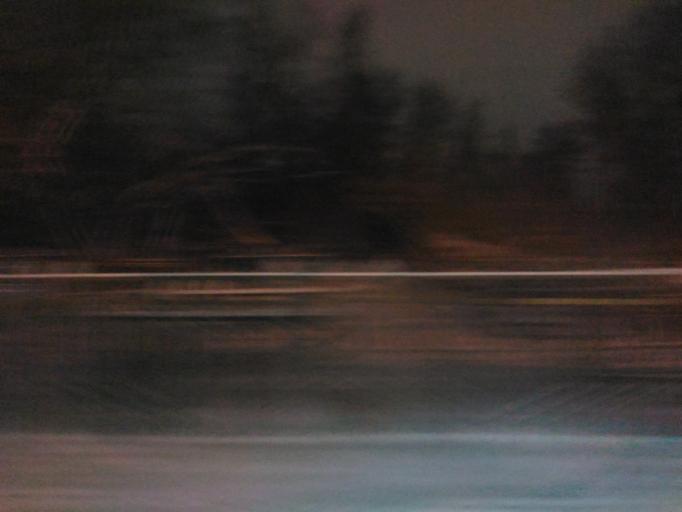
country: RU
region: Ulyanovsk
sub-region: Ulyanovskiy Rayon
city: Ulyanovsk
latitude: 54.3255
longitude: 48.3653
